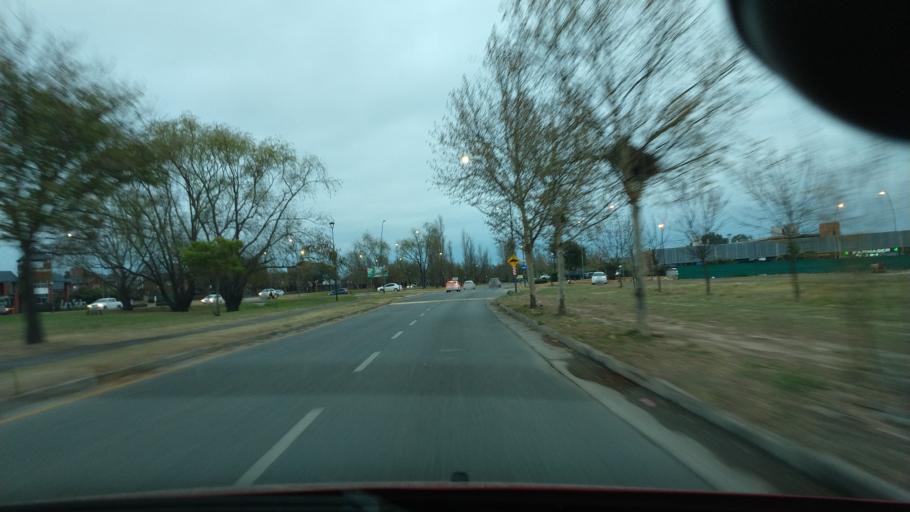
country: AR
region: Cordoba
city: La Calera
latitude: -31.3742
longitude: -64.2774
